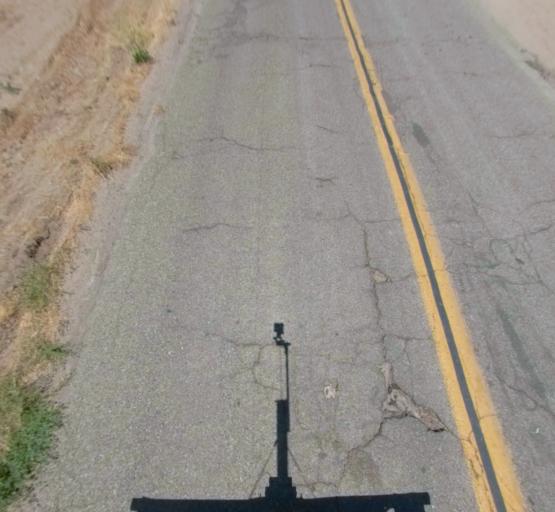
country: US
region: California
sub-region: Madera County
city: Parkwood
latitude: 36.8590
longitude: -120.1103
